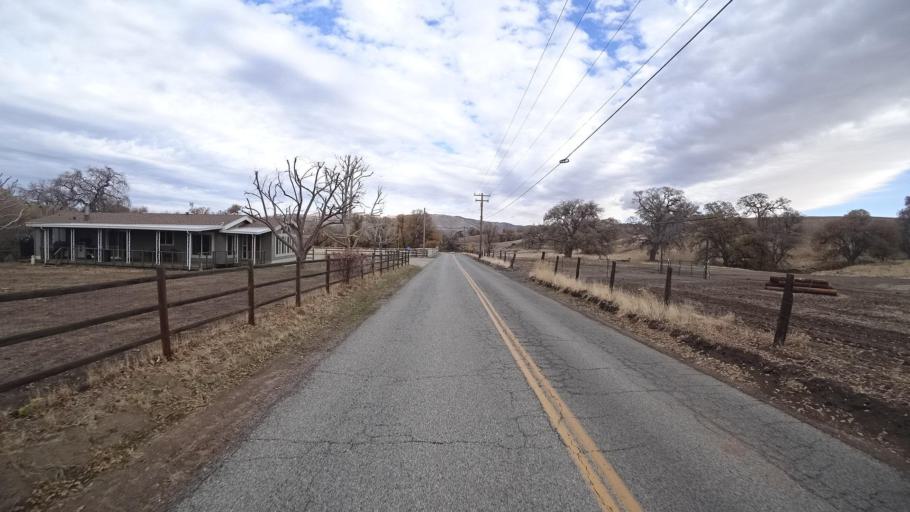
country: US
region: California
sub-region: Kern County
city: Golden Hills
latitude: 35.1367
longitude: -118.5023
